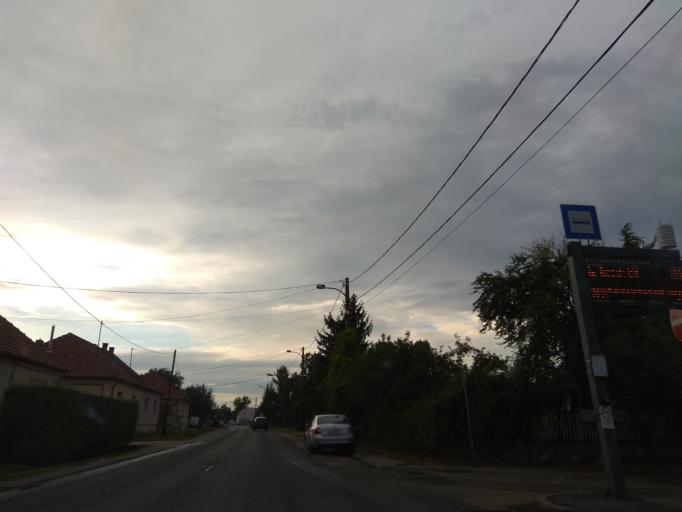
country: HU
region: Borsod-Abauj-Zemplen
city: Miskolc
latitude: 48.0871
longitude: 20.8158
